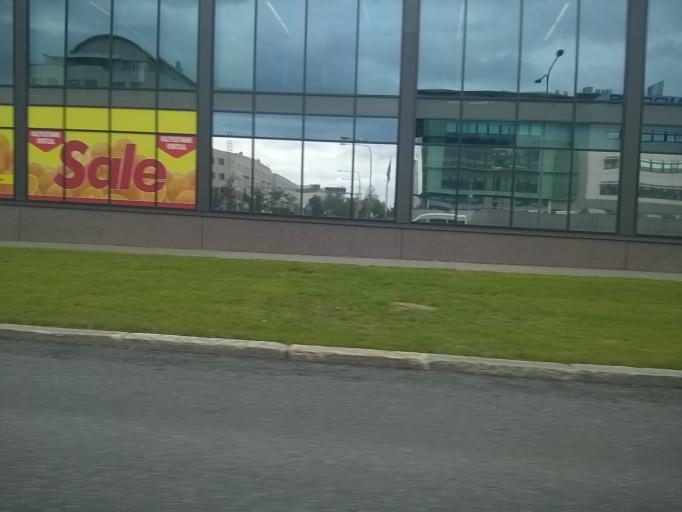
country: FI
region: Pirkanmaa
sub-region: Tampere
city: Tampere
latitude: 61.4464
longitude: 23.8554
